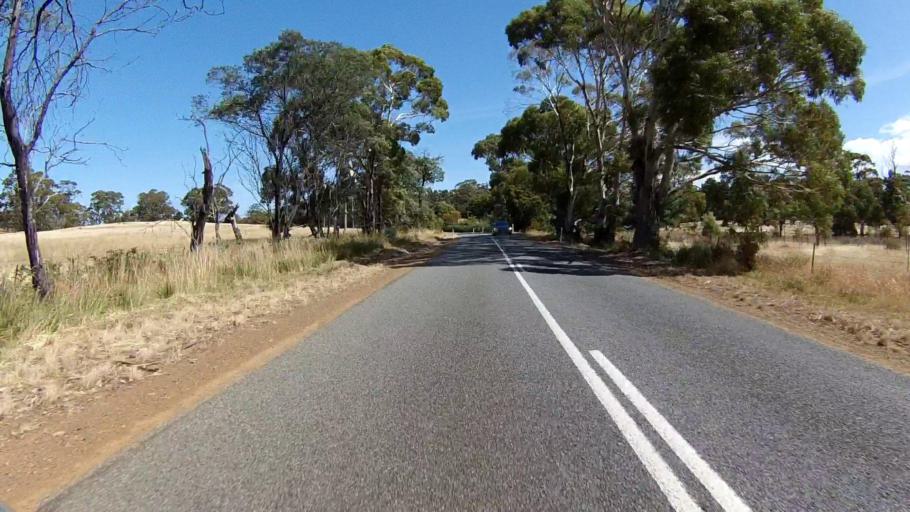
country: AU
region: Tasmania
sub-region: Sorell
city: Sorell
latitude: -42.3067
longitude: 147.9646
